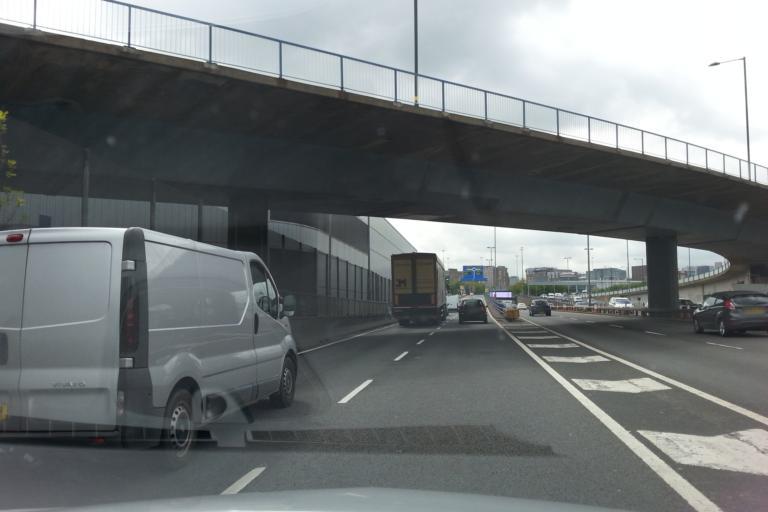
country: GB
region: England
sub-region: City and Borough of Birmingham
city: Birmingham
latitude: 52.4962
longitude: -1.8869
